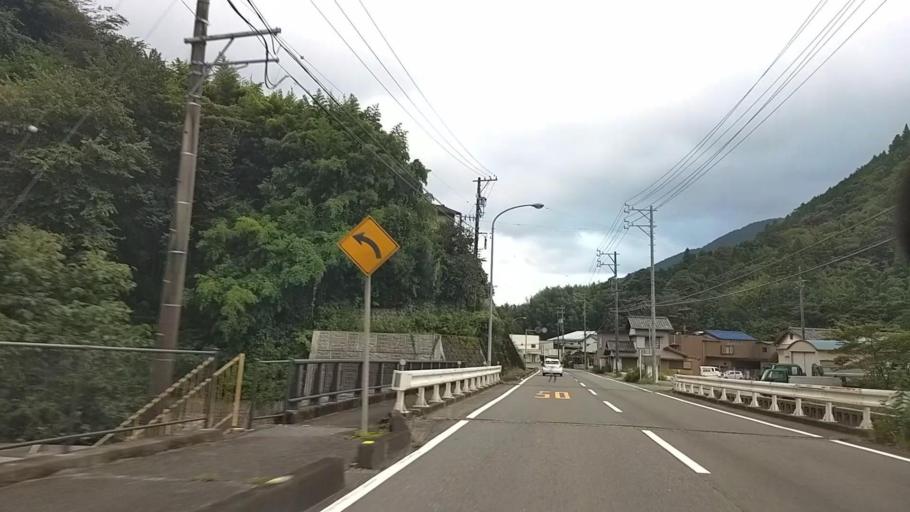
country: JP
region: Shizuoka
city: Fujinomiya
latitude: 35.1143
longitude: 138.5128
